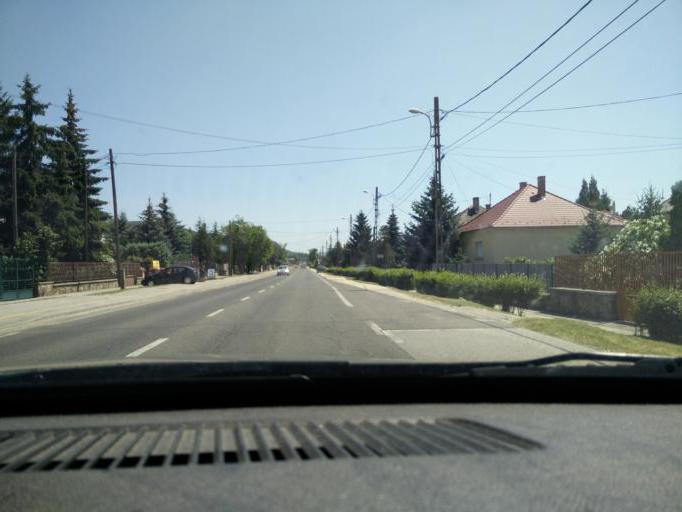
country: HU
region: Komarom-Esztergom
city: Vertesszolos
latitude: 47.6162
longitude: 18.3795
